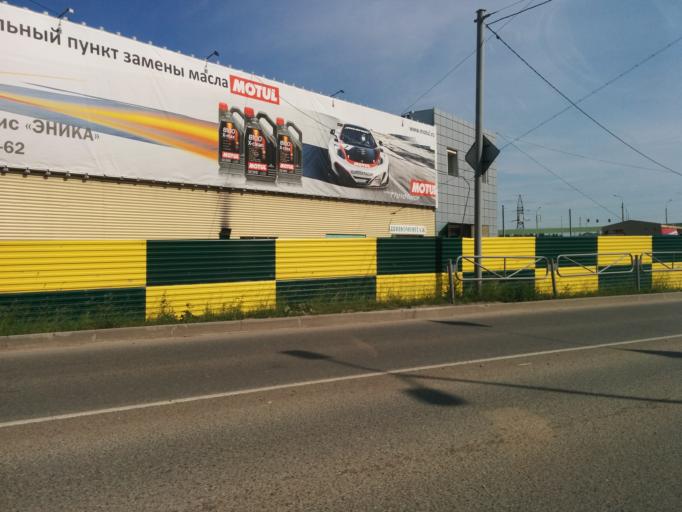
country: RU
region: Perm
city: Perm
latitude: 58.0023
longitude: 56.3136
